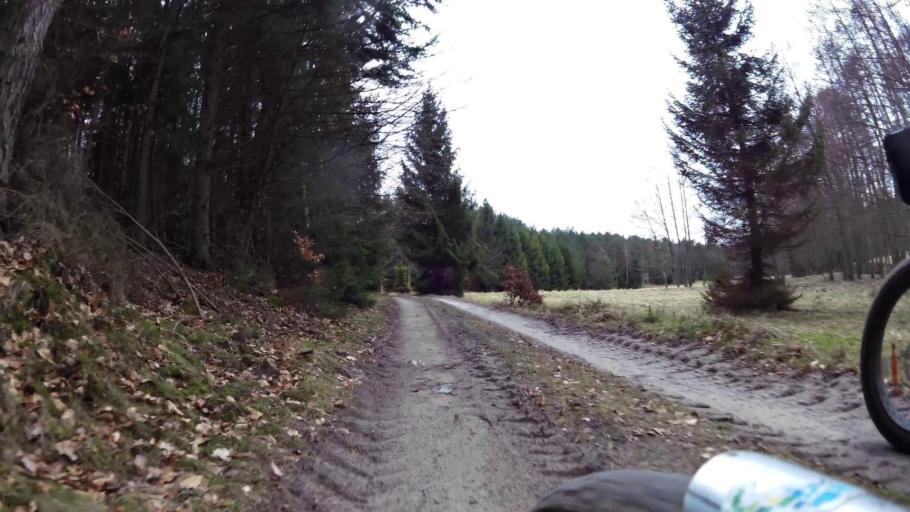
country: PL
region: Pomeranian Voivodeship
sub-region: Powiat bytowski
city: Trzebielino
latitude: 54.1282
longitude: 17.1352
